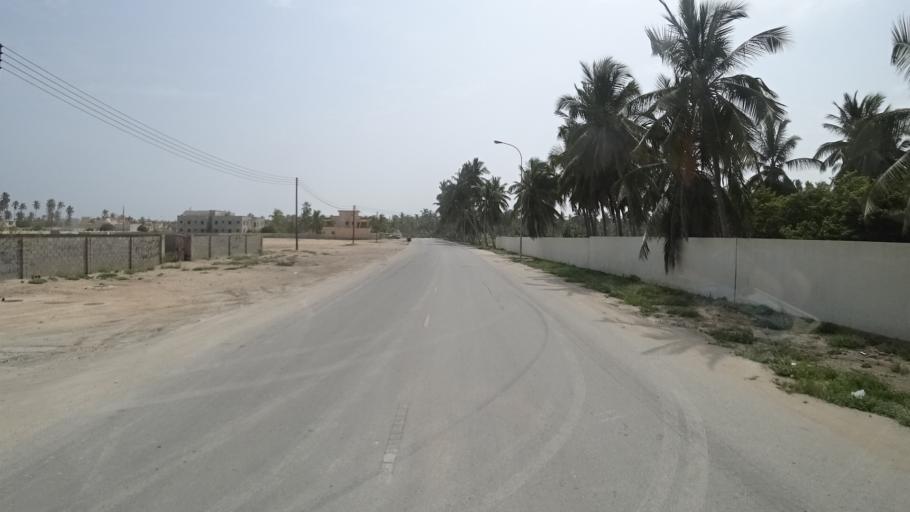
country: OM
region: Zufar
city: Salalah
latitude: 17.0114
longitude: 54.1560
